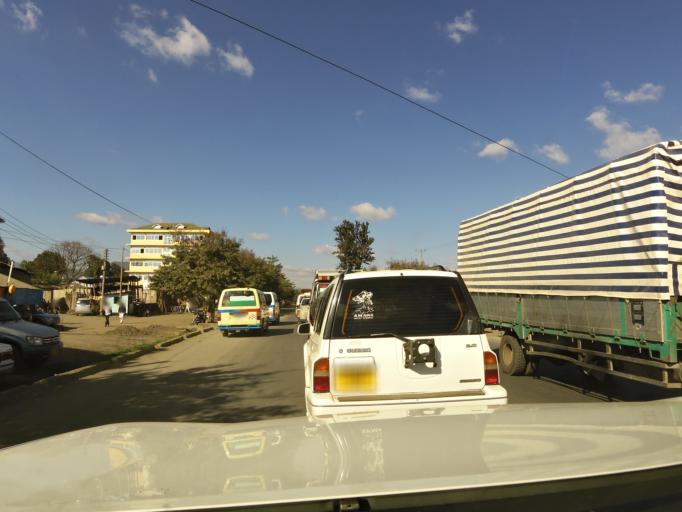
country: TZ
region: Arusha
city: Arusha
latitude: -3.3759
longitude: 36.6669
